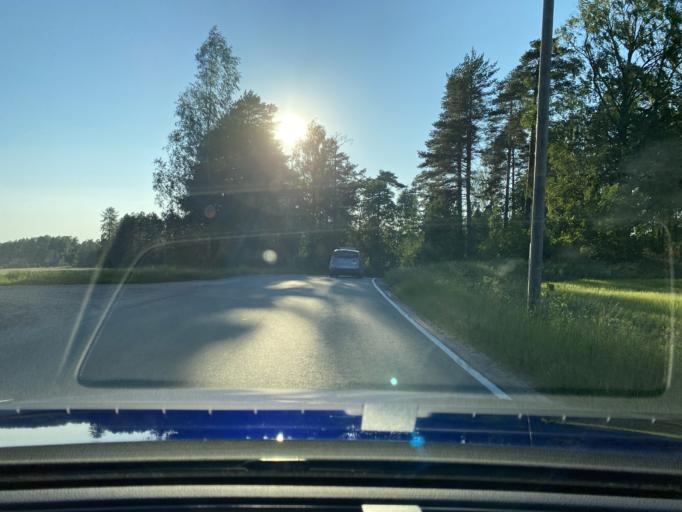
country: FI
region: Haeme
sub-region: Haemeenlinna
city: Tervakoski
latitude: 60.7413
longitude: 24.6522
